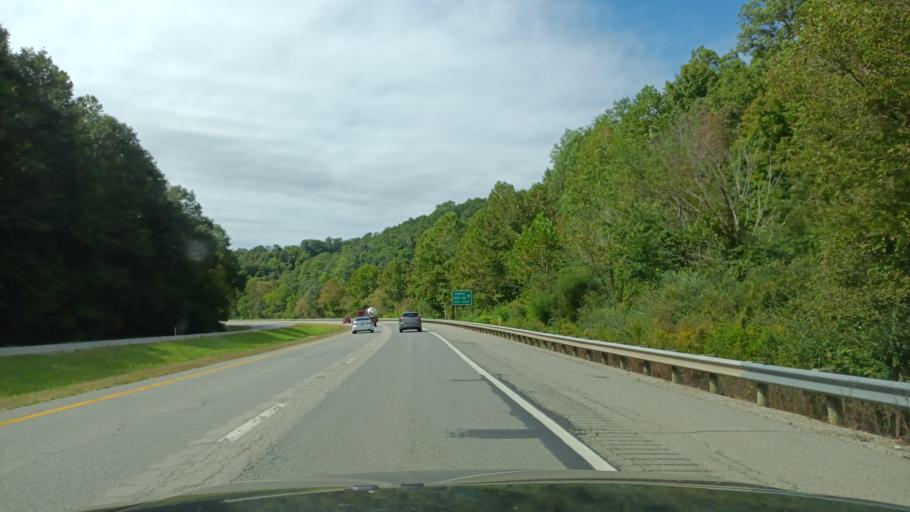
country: US
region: West Virginia
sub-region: Pleasants County
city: Saint Marys
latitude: 39.2554
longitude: -81.1879
